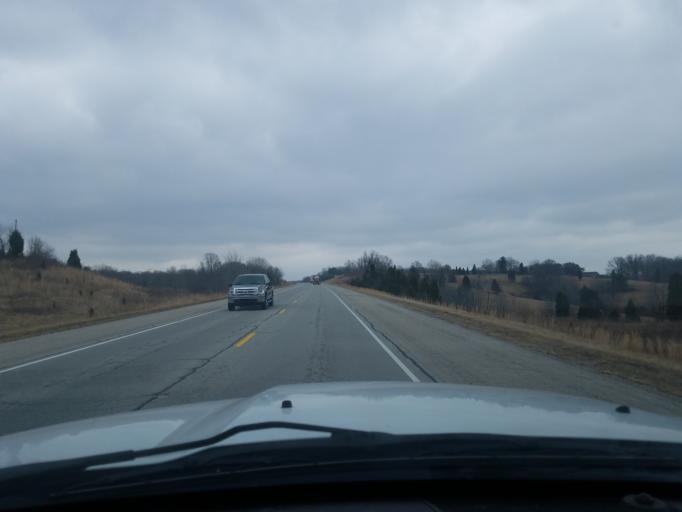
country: US
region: Indiana
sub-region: Perry County
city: Tell City
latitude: 38.0482
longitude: -86.6424
